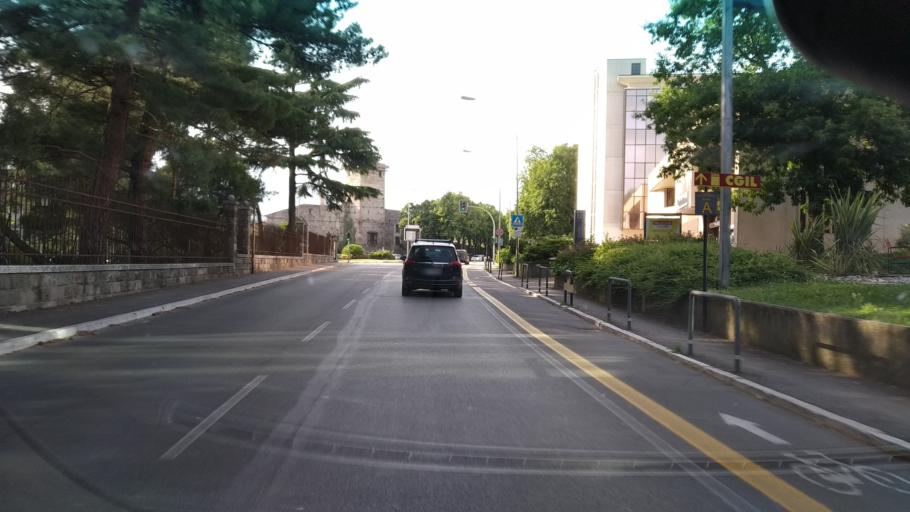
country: IT
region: Veneto
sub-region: Provincia di Vicenza
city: Bassano del Grappa
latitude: 45.7648
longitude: 11.7389
